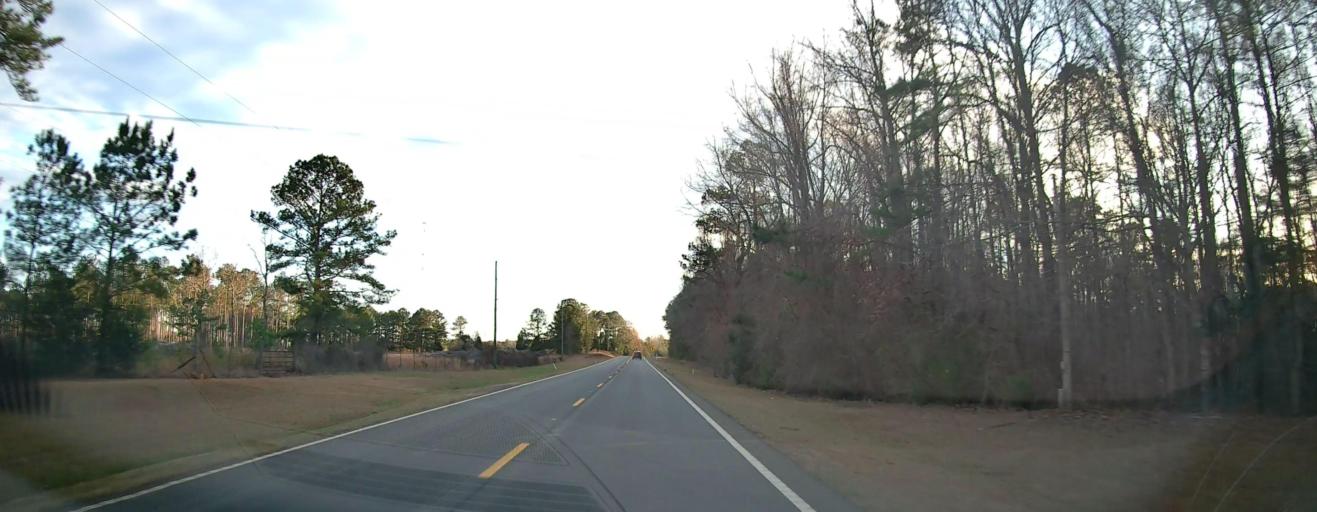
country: US
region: Georgia
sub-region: Talbot County
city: Sardis
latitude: 32.7008
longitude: -84.6998
